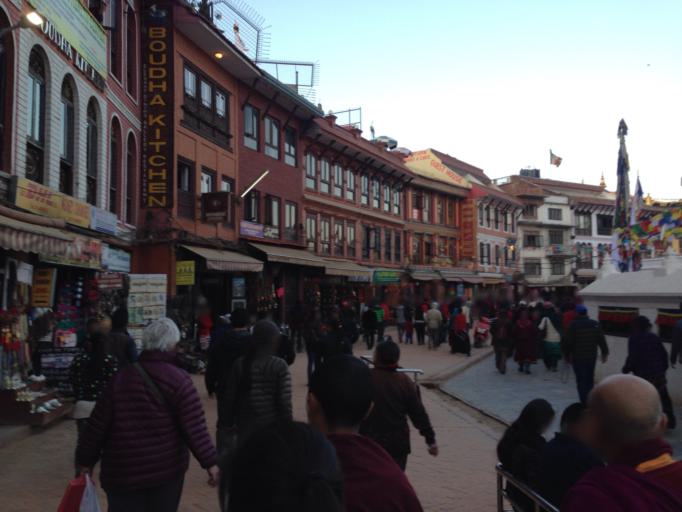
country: NP
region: Central Region
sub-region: Bagmati Zone
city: Kathmandu
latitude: 27.7216
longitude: 85.3614
